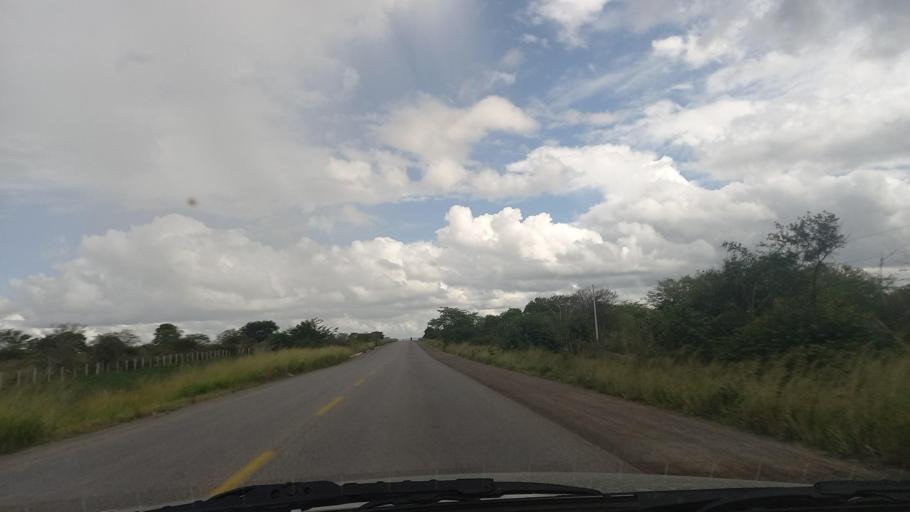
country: BR
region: Pernambuco
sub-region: Cachoeirinha
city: Cachoeirinha
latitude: -8.5427
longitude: -36.2693
